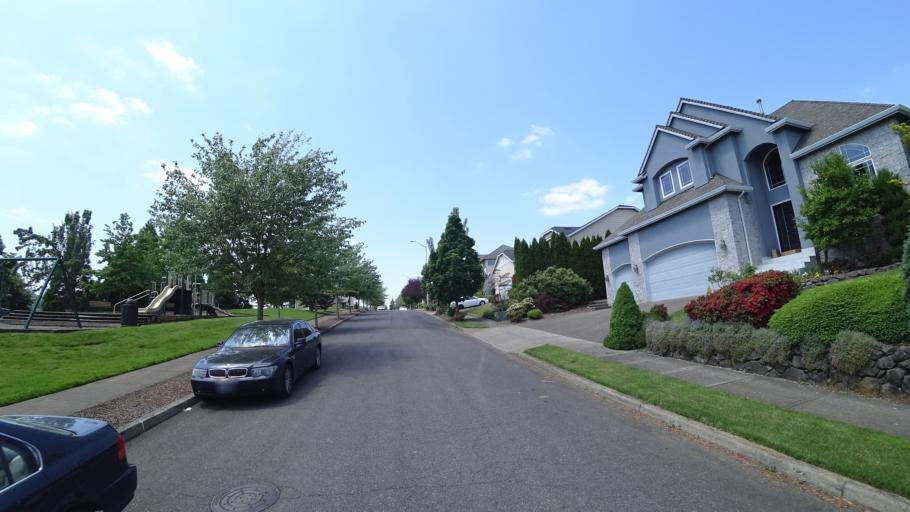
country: US
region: Oregon
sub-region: Clackamas County
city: Happy Valley
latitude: 45.4703
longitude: -122.5027
